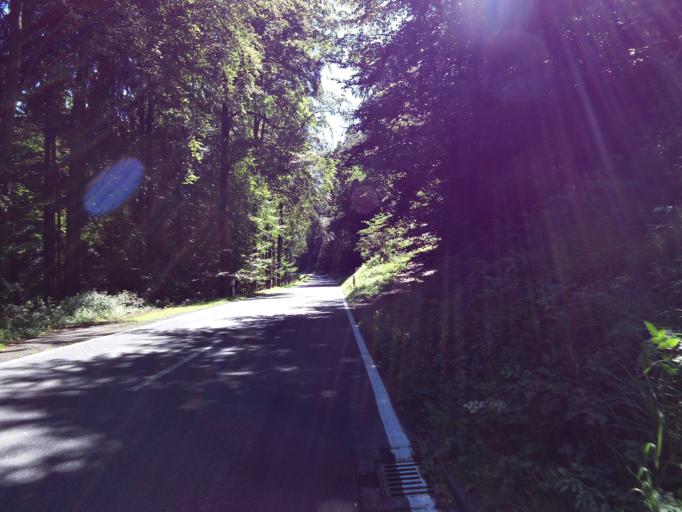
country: DE
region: Hesse
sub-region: Regierungsbezirk Darmstadt
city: Erbach
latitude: 49.6579
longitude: 8.9693
